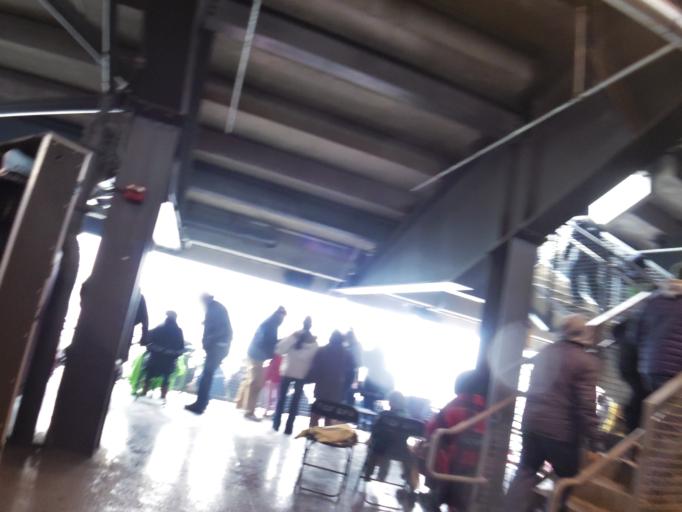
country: US
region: Minnesota
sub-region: Ramsey County
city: Lauderdale
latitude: 44.9772
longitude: -93.2251
